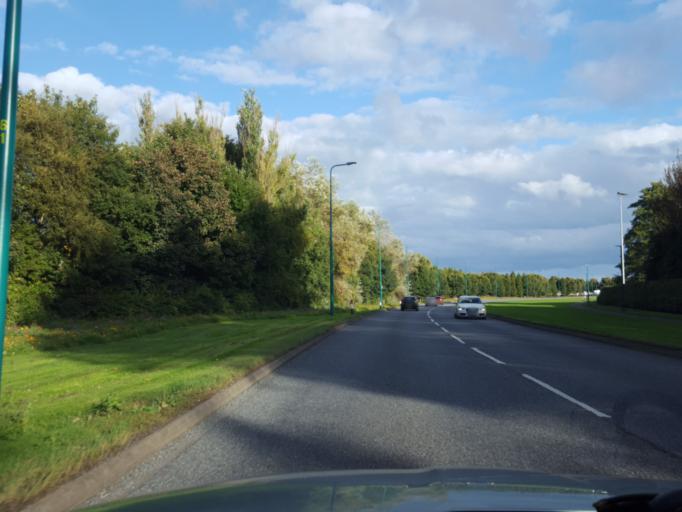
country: GB
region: Scotland
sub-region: Dundee City
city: Dundee
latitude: 56.4545
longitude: -3.0054
